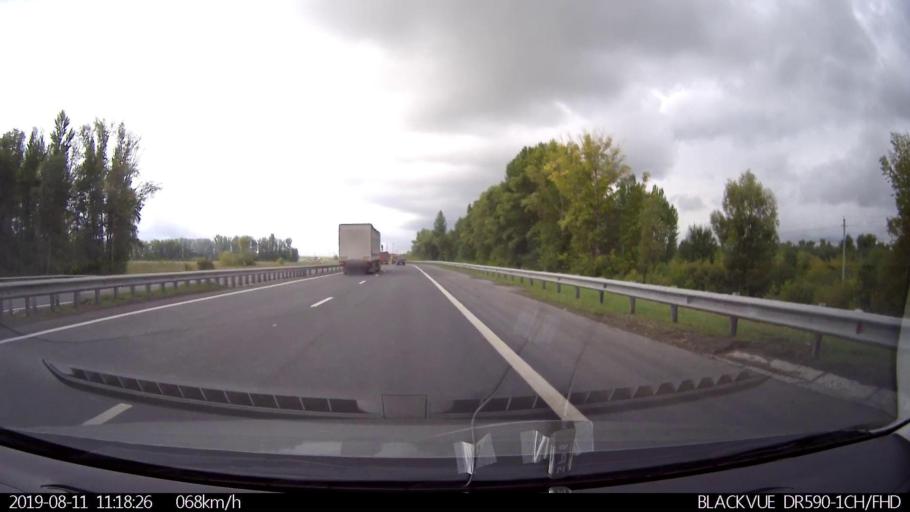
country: RU
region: Ulyanovsk
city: Novoul'yanovsk
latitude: 54.1799
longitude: 48.2683
